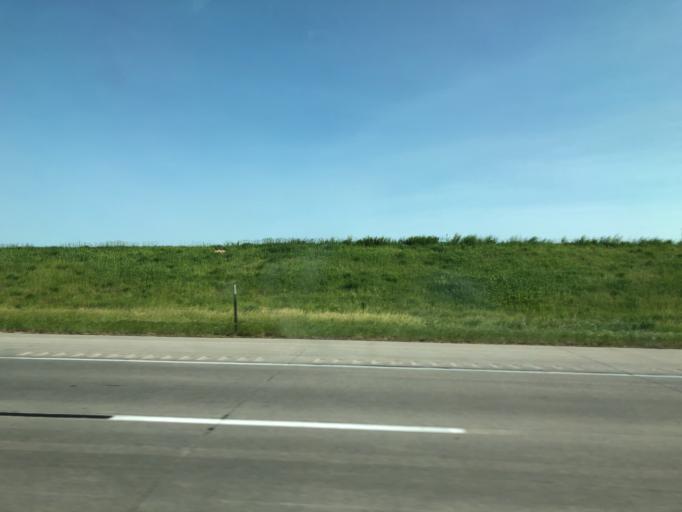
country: US
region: Nebraska
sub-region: Lancaster County
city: Waverly
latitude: 40.9067
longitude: -96.5062
